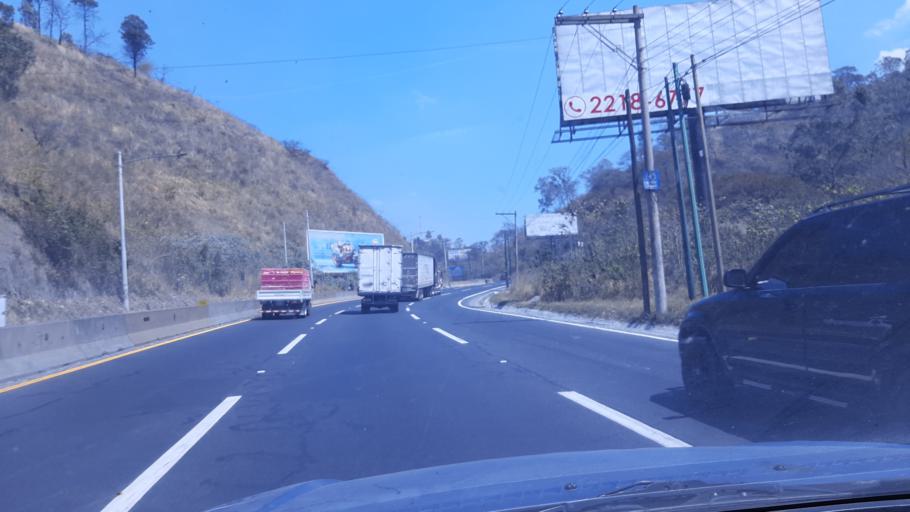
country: GT
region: Guatemala
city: Amatitlan
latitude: 14.5029
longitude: -90.6274
